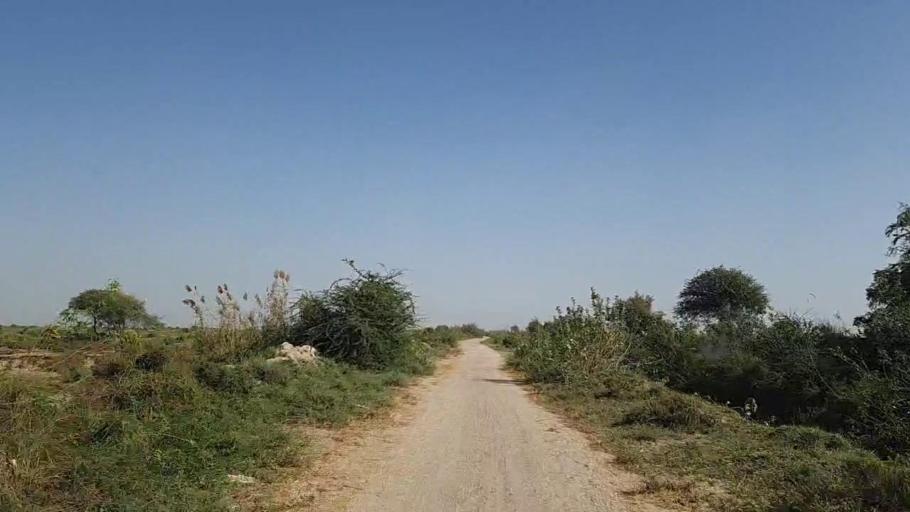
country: PK
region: Sindh
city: Chuhar Jamali
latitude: 24.4841
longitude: 68.0978
